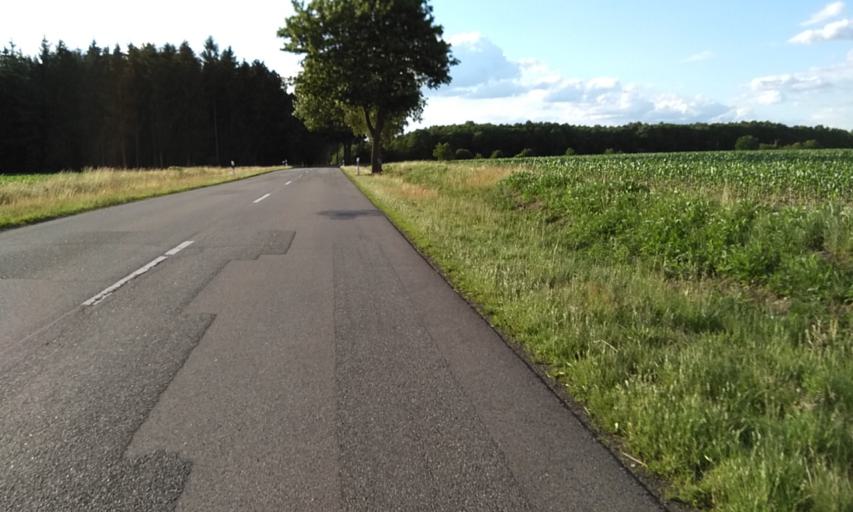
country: DE
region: Lower Saxony
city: Heeslingen
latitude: 53.3539
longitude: 9.3447
